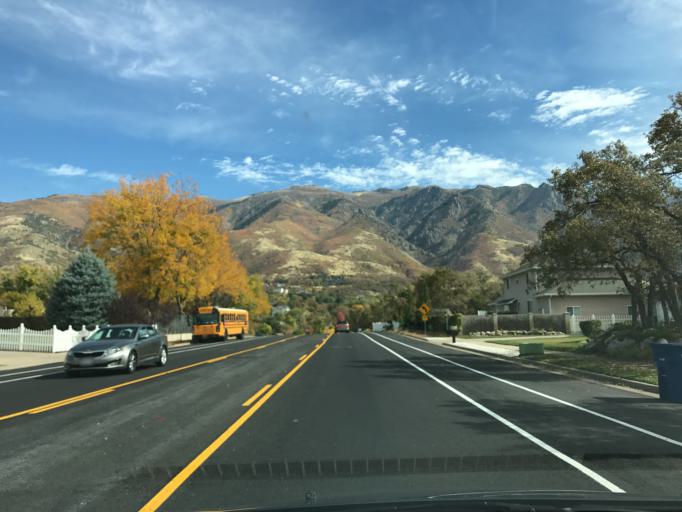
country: US
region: Utah
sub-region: Davis County
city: South Weber
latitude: 41.0891
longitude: -111.9221
